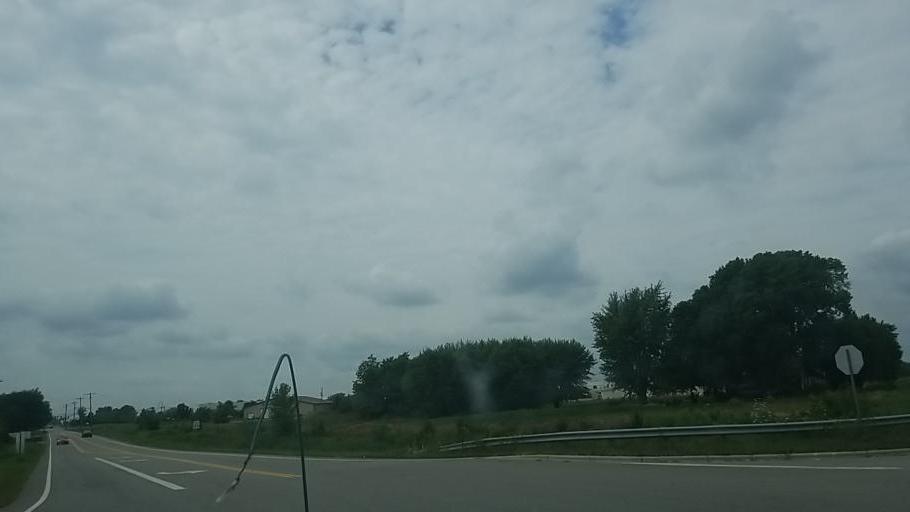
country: US
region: Ohio
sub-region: Franklin County
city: Groveport
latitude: 39.8397
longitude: -82.9039
